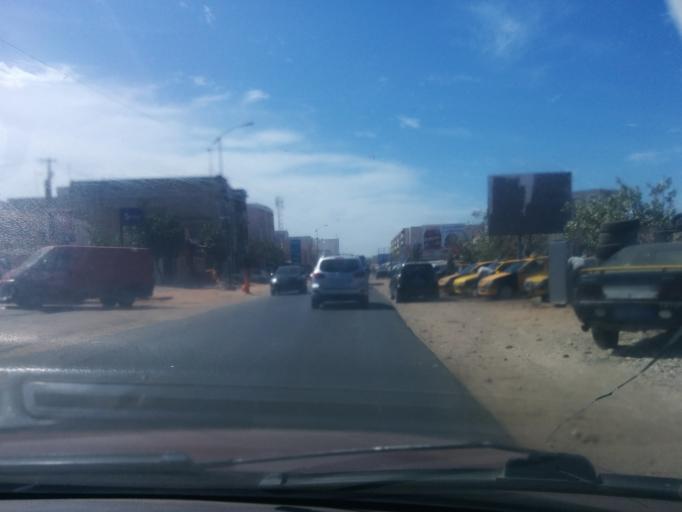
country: SN
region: Dakar
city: Pikine
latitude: 14.7689
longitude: -17.4113
